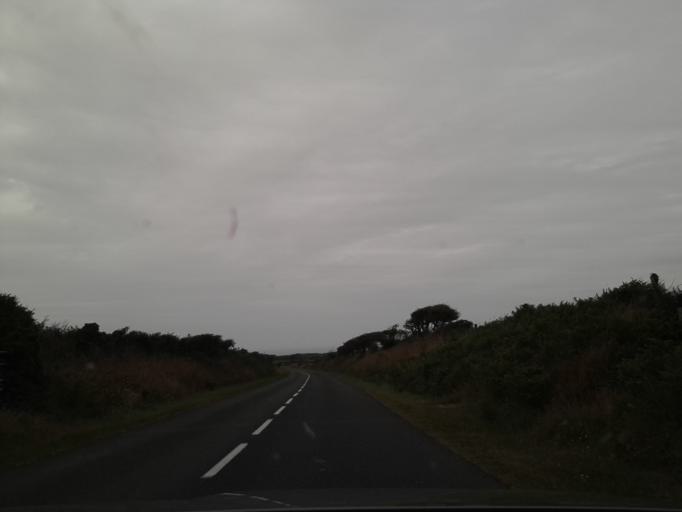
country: FR
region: Lower Normandy
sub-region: Departement de la Manche
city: Beaumont-Hague
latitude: 49.7003
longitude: -1.9269
